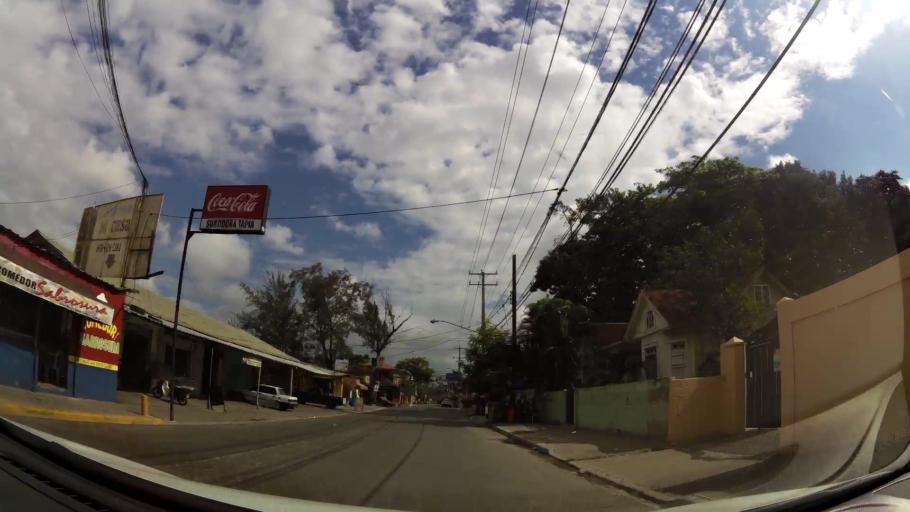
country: DO
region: Santiago
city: Santiago de los Caballeros
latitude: 19.4434
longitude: -70.7069
